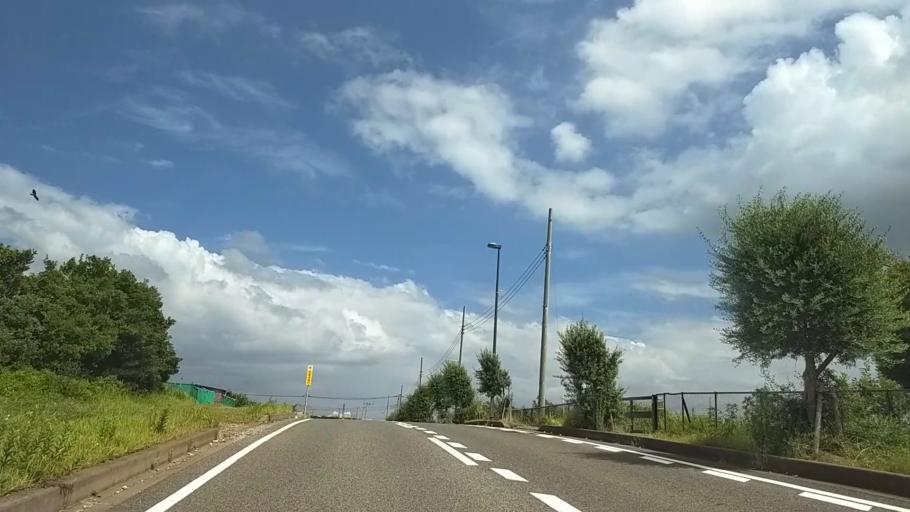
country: JP
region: Kanagawa
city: Miura
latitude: 35.1961
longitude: 139.6132
